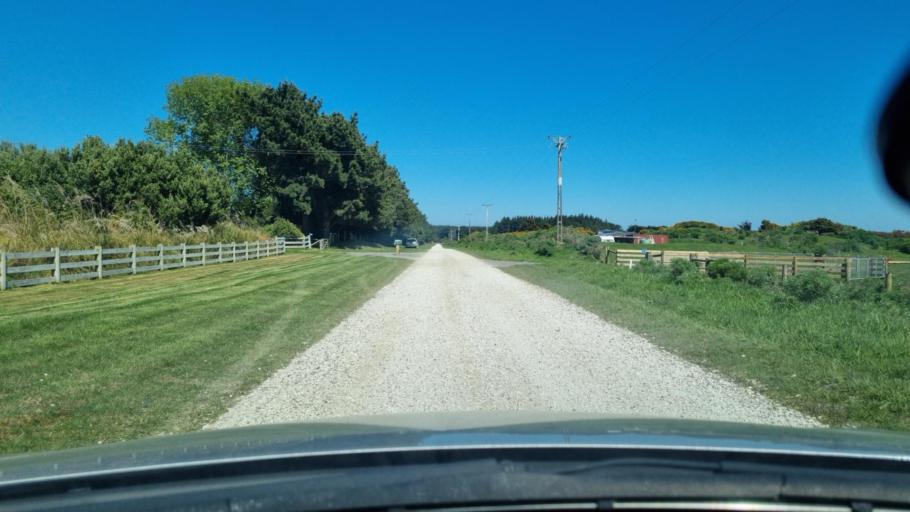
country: NZ
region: Southland
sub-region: Invercargill City
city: Invercargill
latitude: -46.4543
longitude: 168.2761
